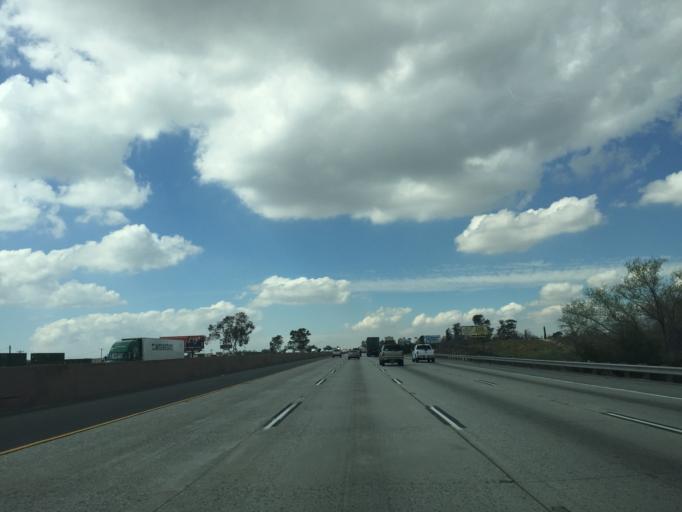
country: US
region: California
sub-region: Riverside County
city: Beaumont
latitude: 33.9266
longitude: -116.9347
